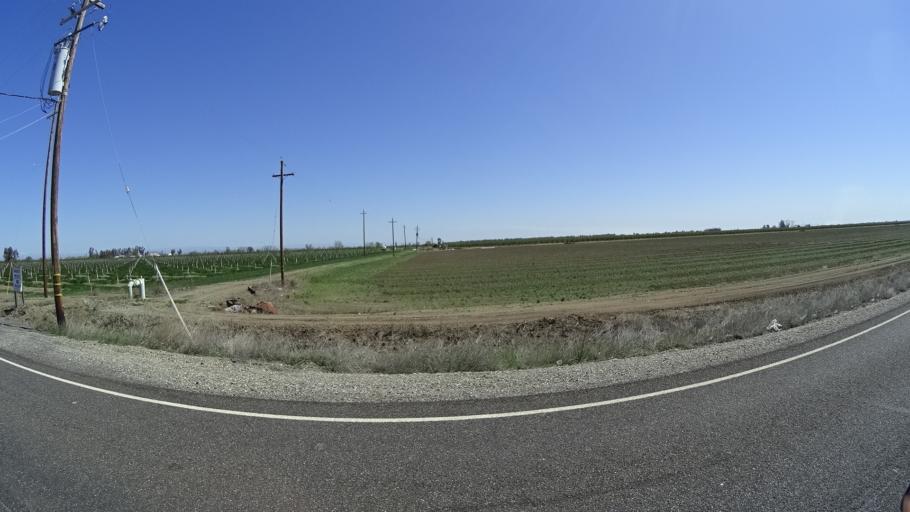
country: US
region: California
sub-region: Glenn County
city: Willows
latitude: 39.5968
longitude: -122.2499
